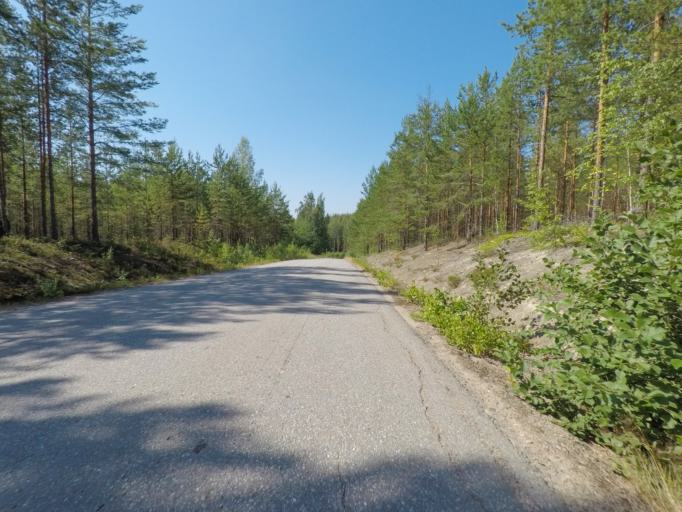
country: FI
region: Southern Savonia
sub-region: Mikkeli
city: Puumala
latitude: 61.4231
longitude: 28.1020
